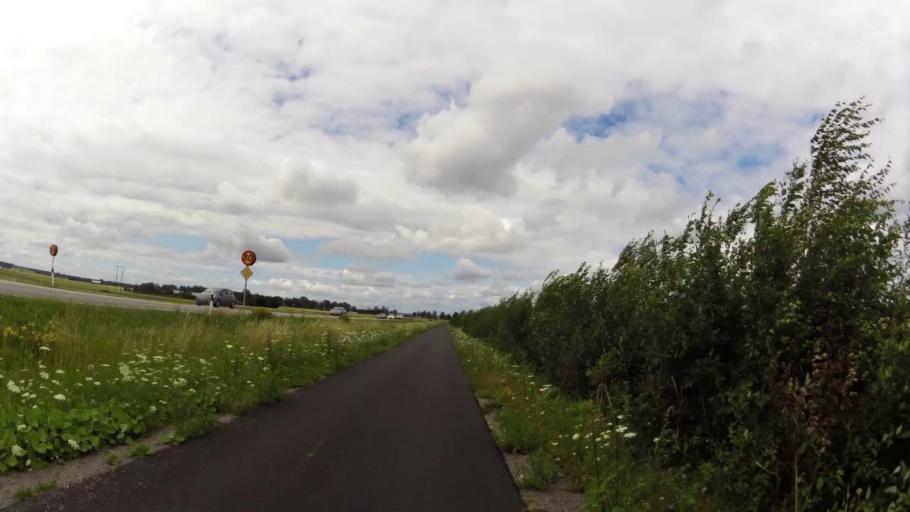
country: SE
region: OEstergoetland
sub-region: Linkopings Kommun
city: Linkoping
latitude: 58.4427
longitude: 15.5742
